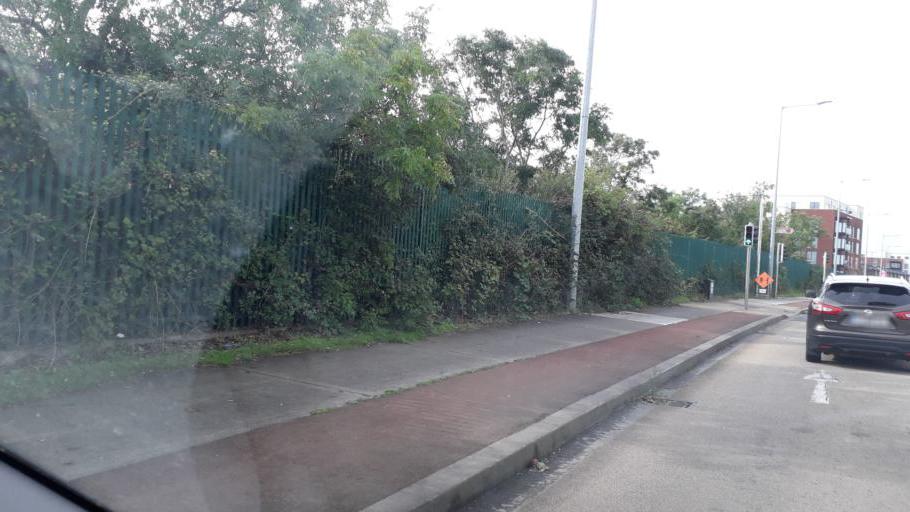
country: IE
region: Leinster
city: Foxrock
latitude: 53.2575
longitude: -6.1964
